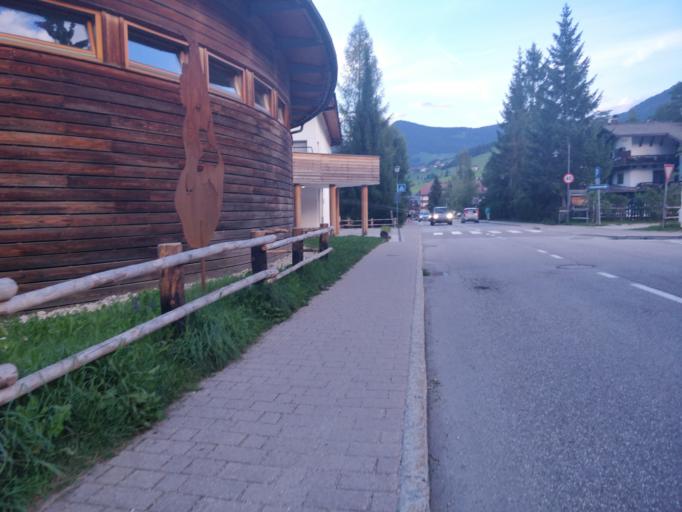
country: IT
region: Trentino-Alto Adige
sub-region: Bolzano
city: San Vigilio
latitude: 46.6946
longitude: 11.9362
